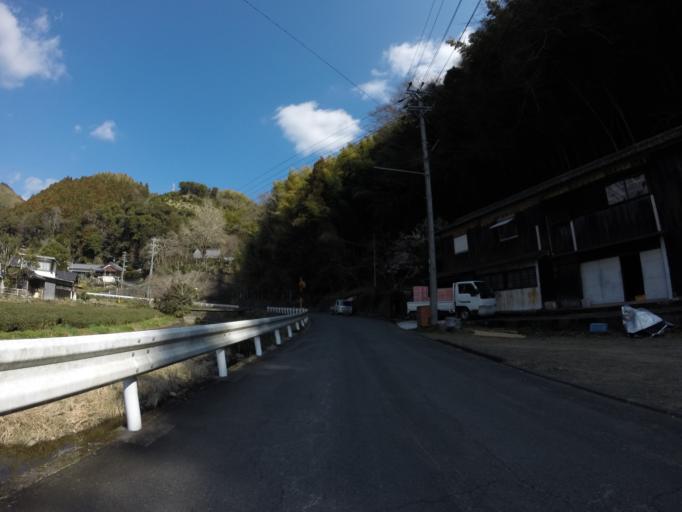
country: JP
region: Shizuoka
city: Shizuoka-shi
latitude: 35.0733
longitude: 138.4849
